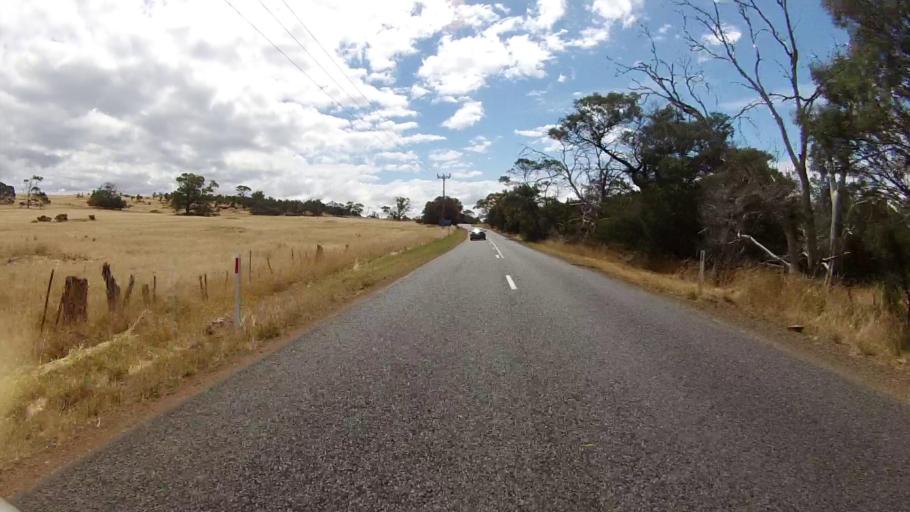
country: AU
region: Tasmania
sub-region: Sorell
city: Sorell
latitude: -42.1622
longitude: 148.0713
